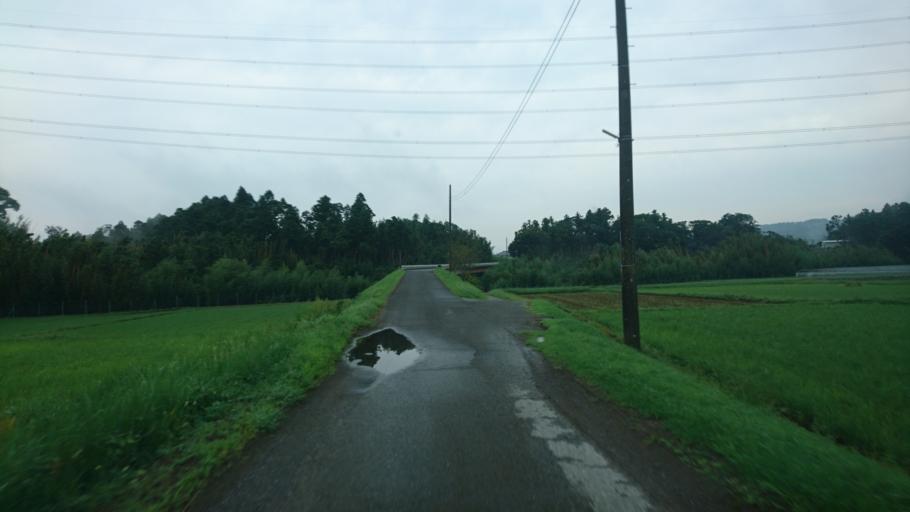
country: JP
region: Chiba
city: Kimitsu
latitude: 35.2841
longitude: 139.9850
